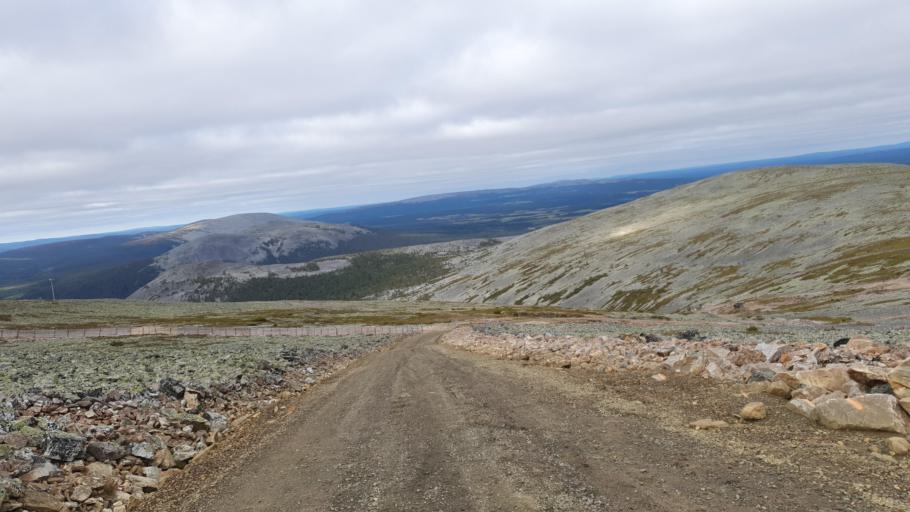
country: FI
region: Lapland
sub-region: Tunturi-Lappi
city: Kolari
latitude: 67.5698
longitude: 24.2147
